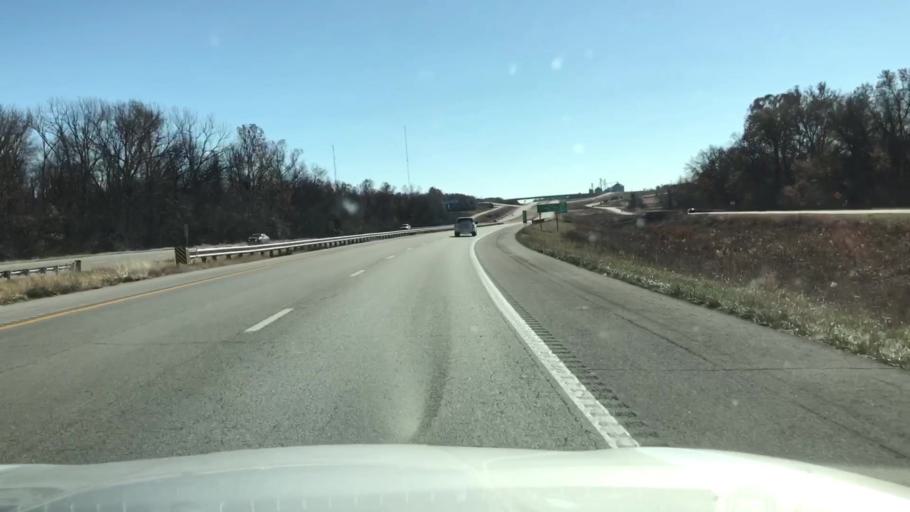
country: US
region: Missouri
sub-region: Jasper County
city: Carthage
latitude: 37.1081
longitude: -94.3101
